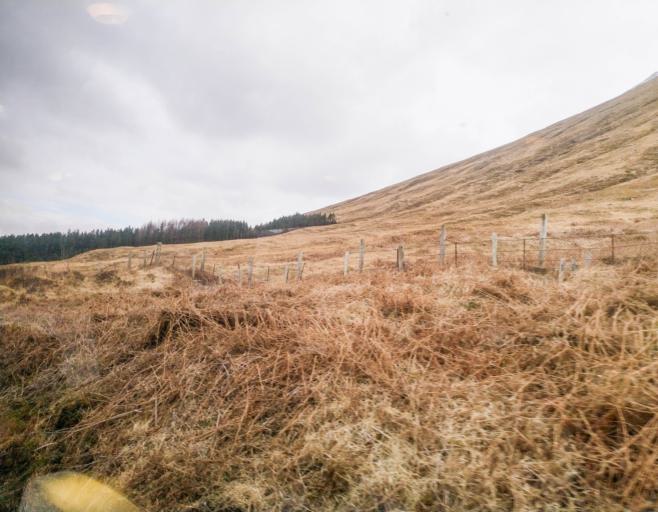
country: GB
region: Scotland
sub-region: Argyll and Bute
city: Garelochhead
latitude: 56.4949
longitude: -4.7408
